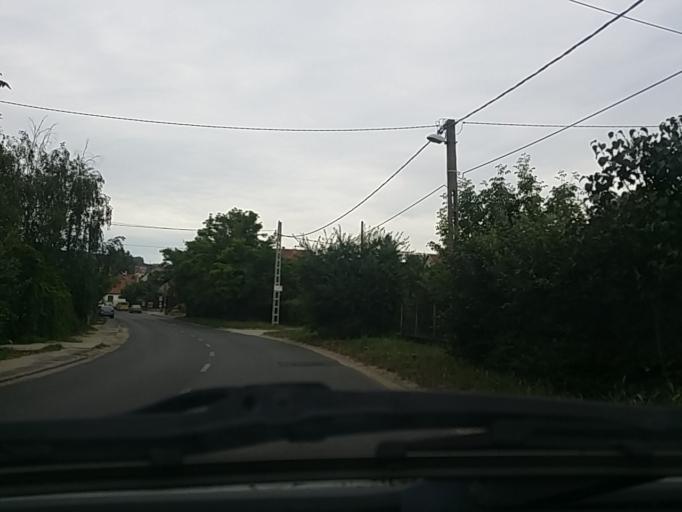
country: HU
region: Pest
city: Urom
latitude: 47.5940
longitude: 19.0123
